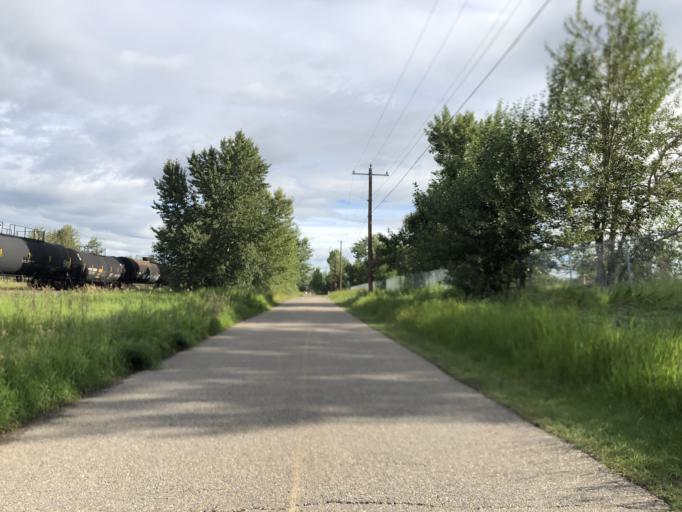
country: CA
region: Alberta
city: Calgary
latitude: 51.0287
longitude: -114.0113
